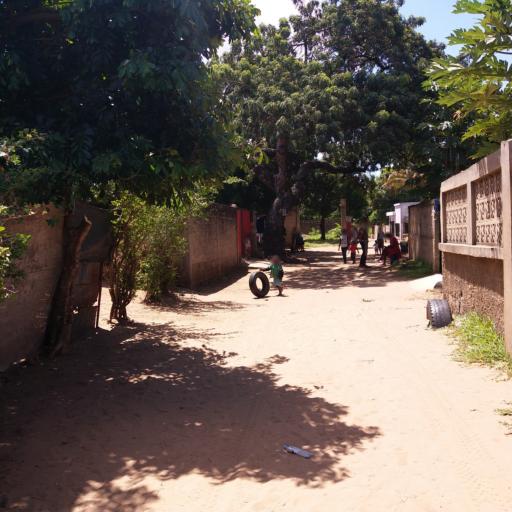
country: MZ
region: Maputo City
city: Maputo
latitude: -25.9027
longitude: 32.5912
